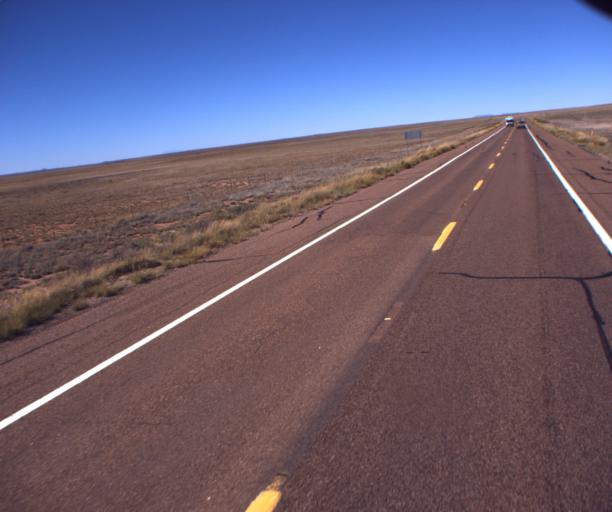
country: US
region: Arizona
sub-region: Navajo County
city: Holbrook
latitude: 34.8156
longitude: -109.9223
